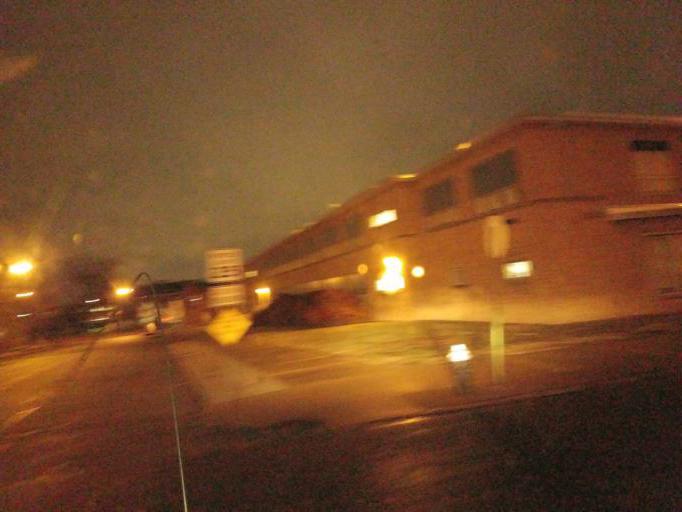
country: US
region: Missouri
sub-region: City of Saint Louis
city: St. Louis
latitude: 38.6520
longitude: -90.1953
